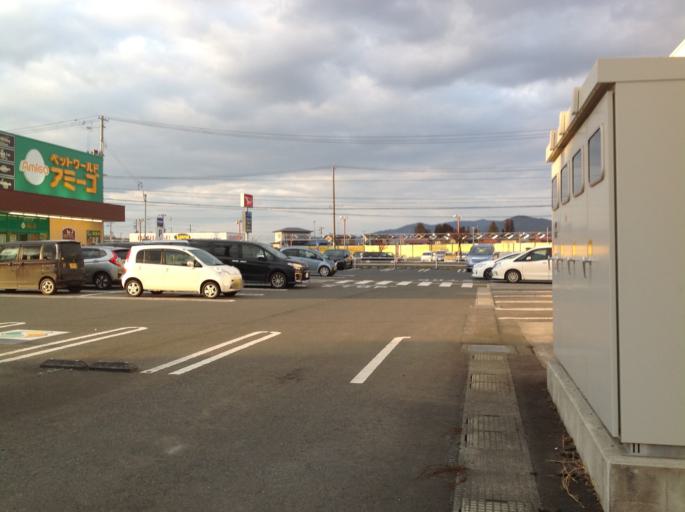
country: JP
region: Iwate
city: Ichinoseki
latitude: 38.9388
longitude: 141.1493
